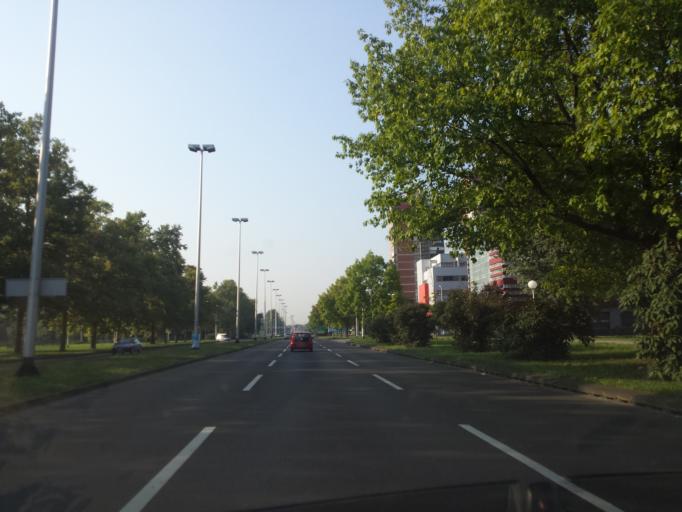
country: HR
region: Grad Zagreb
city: Novi Zagreb
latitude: 45.7761
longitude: 15.9905
